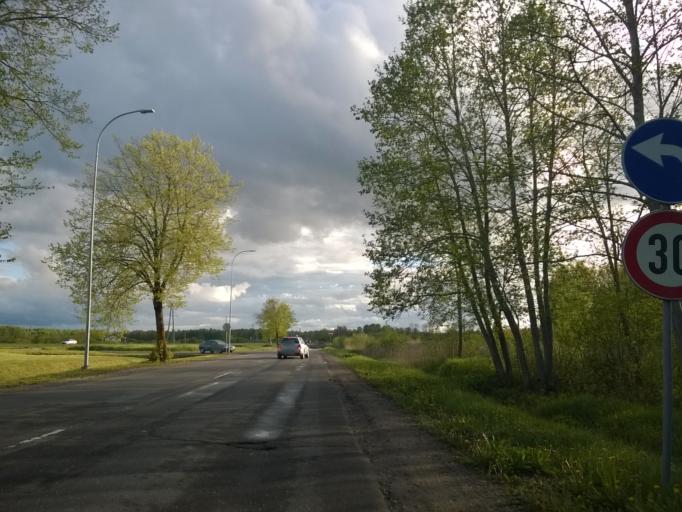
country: LV
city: Tireli
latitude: 56.9309
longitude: 23.5870
